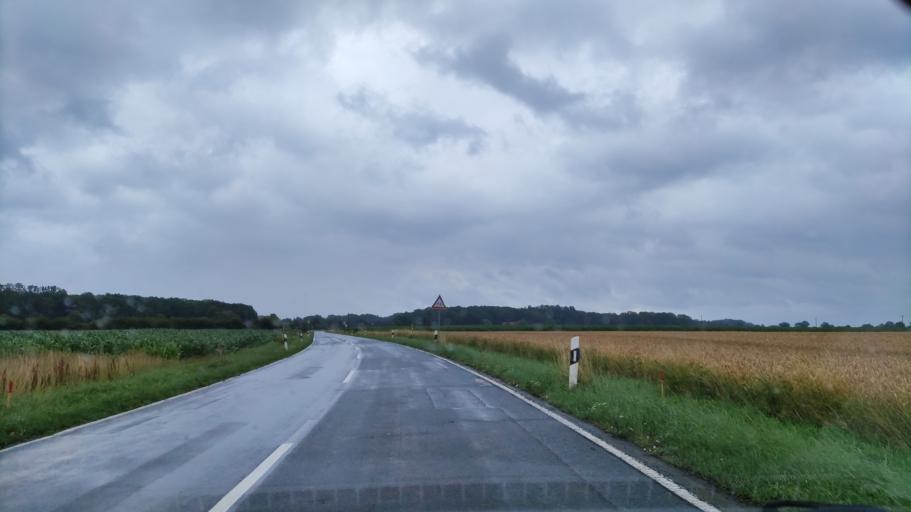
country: DE
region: North Rhine-Westphalia
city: Sendenhorst
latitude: 51.8907
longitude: 7.7797
